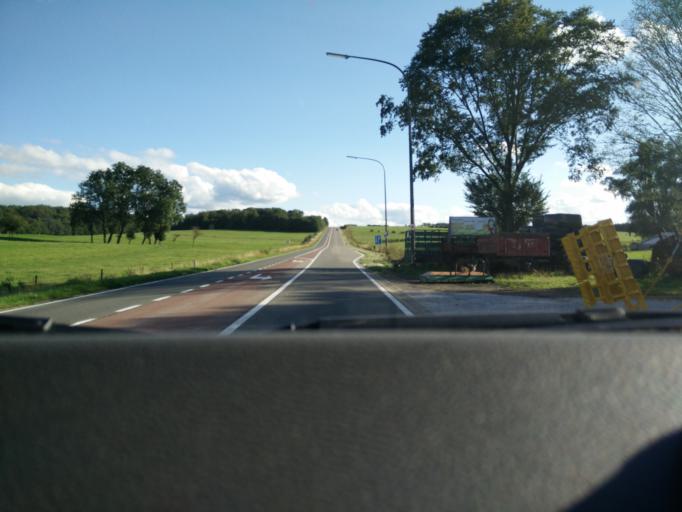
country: BE
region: Wallonia
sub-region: Province du Hainaut
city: Beaumont
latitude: 50.2161
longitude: 4.2267
